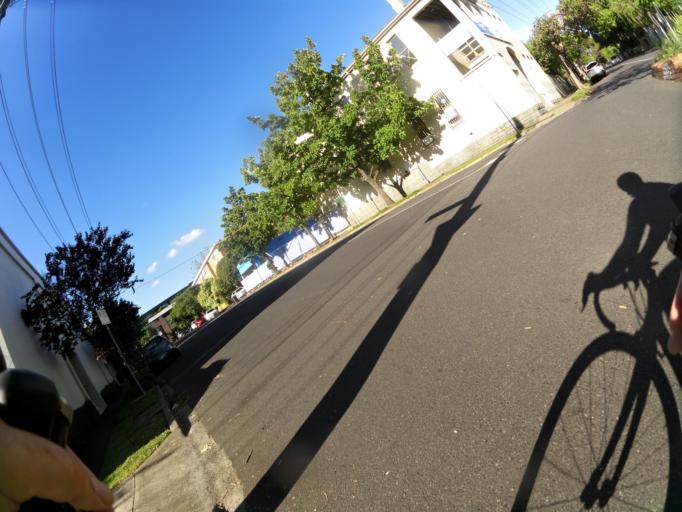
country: AU
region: Victoria
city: Toorak
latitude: -37.8511
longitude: 145.0180
